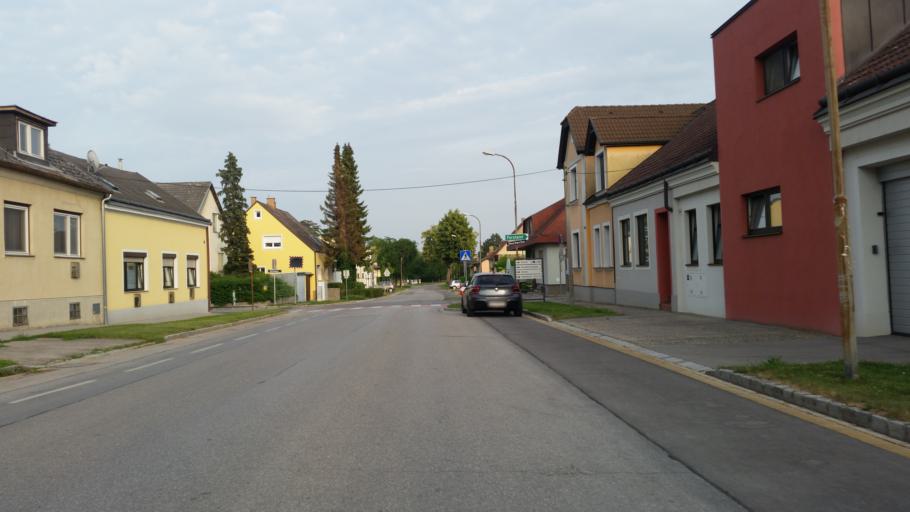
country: AT
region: Lower Austria
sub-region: Politischer Bezirk Mistelbach
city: Wolkersdorf im Weinviertel
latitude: 48.3836
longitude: 16.5221
